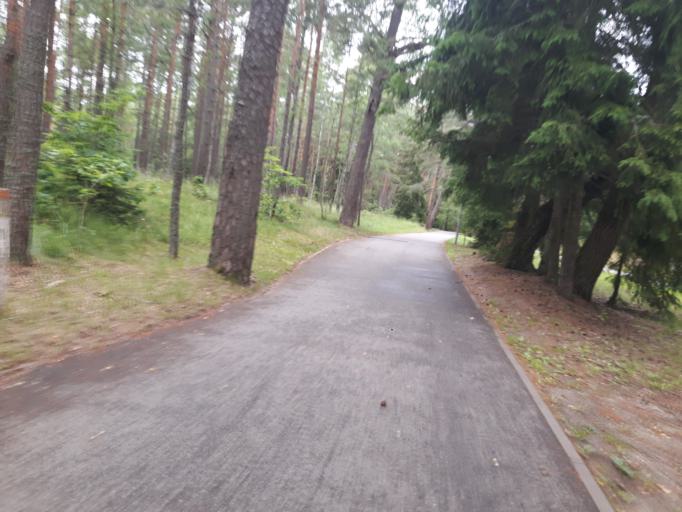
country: LT
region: Klaipedos apskritis
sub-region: Klaipeda
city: Klaipeda
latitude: 55.7411
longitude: 21.1241
